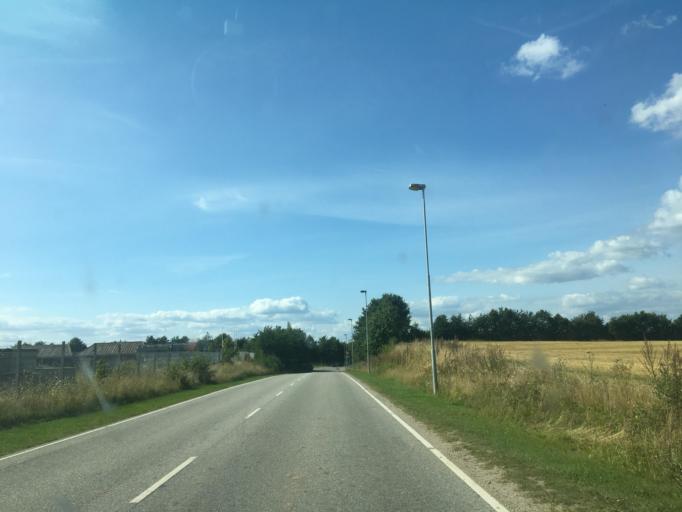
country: DK
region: South Denmark
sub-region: Middelfart Kommune
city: Ejby
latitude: 55.3970
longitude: 9.9679
